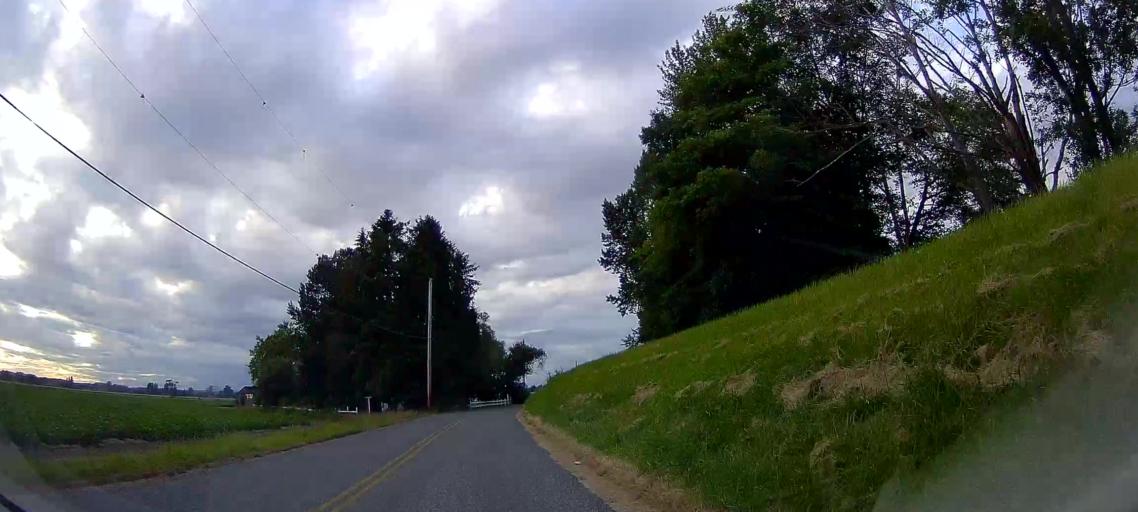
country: US
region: Washington
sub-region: Skagit County
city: Mount Vernon
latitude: 48.3502
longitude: -122.3614
